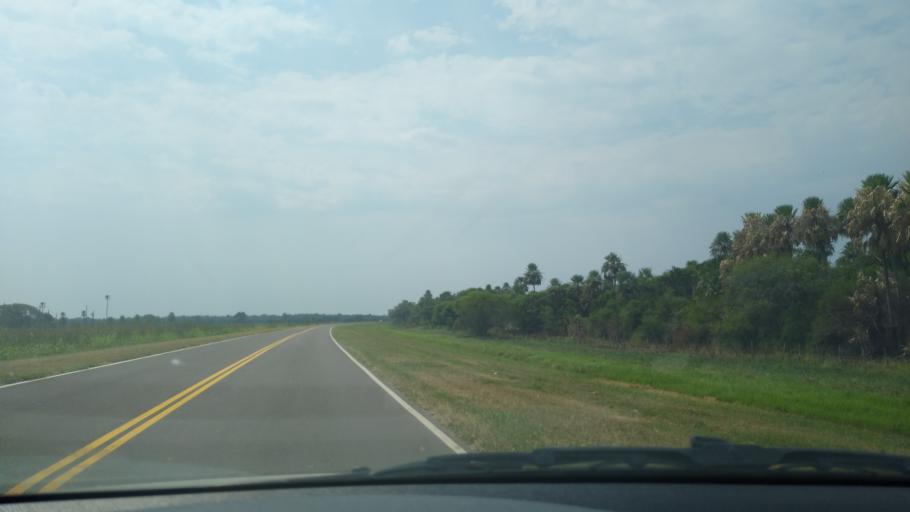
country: AR
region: Chaco
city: Margarita Belen
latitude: -27.0715
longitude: -58.9627
